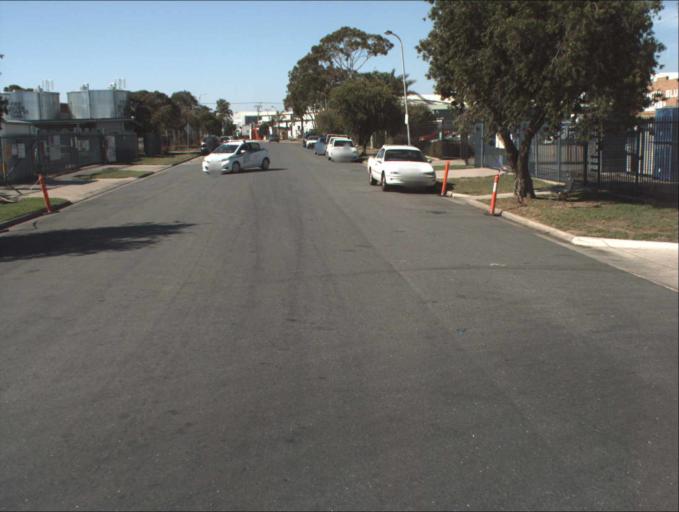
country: AU
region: South Australia
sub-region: Port Adelaide Enfield
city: Blair Athol
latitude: -34.8417
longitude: 138.5801
